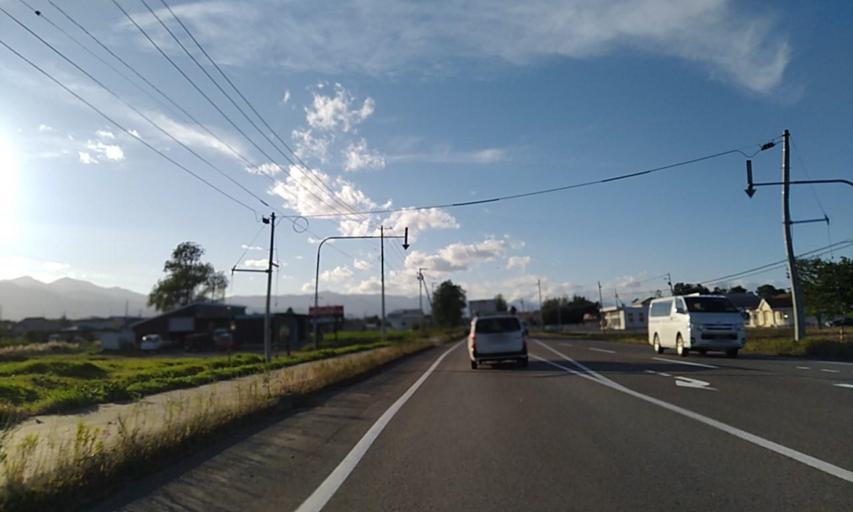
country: JP
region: Hokkaido
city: Otofuke
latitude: 42.9427
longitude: 142.9499
